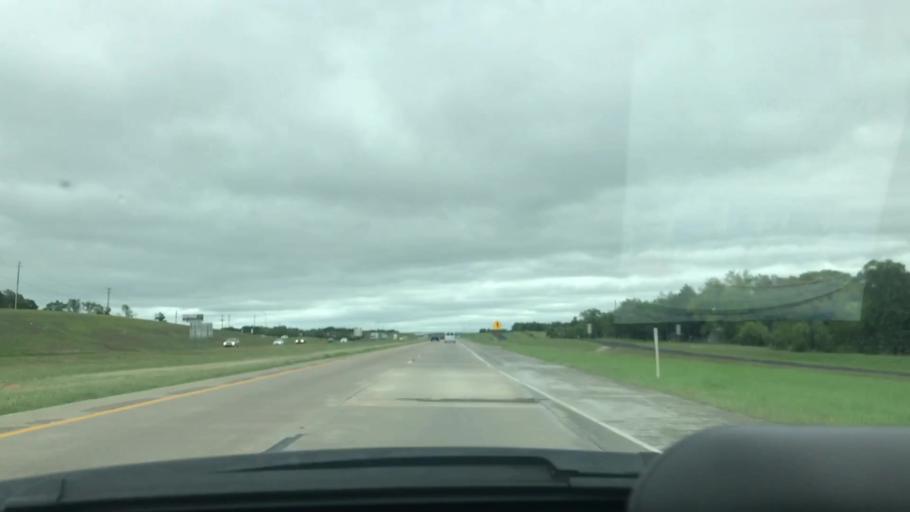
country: US
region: Texas
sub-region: Grayson County
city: Sherman
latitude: 33.6827
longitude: -96.6066
